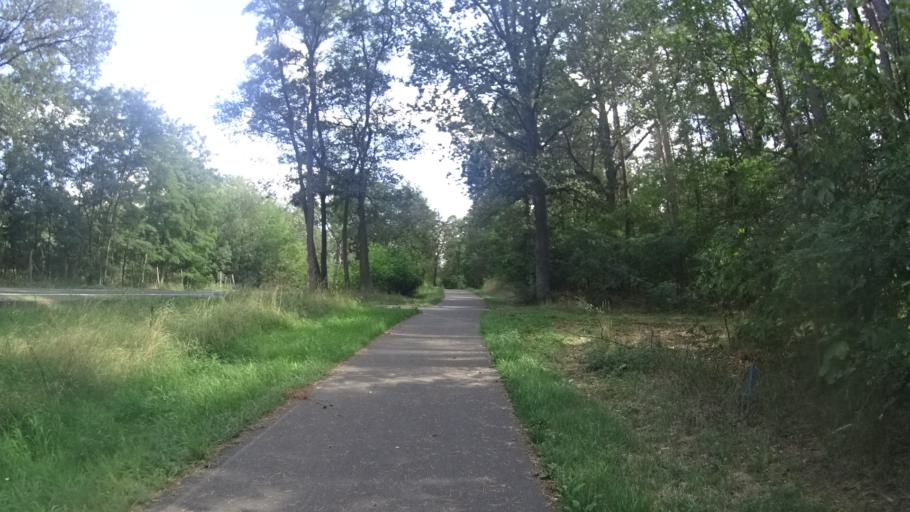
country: DE
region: Brandenburg
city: Rhinow
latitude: 52.7162
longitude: 12.3663
